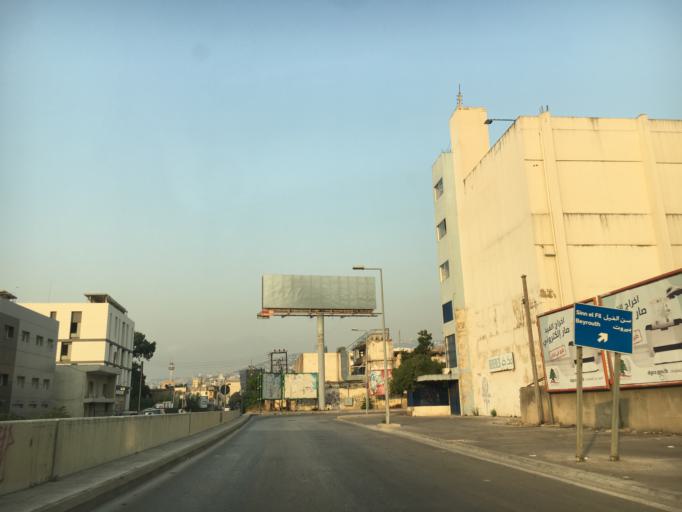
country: LB
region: Mont-Liban
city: Jdaidet el Matn
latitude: 33.9005
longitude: 35.5665
